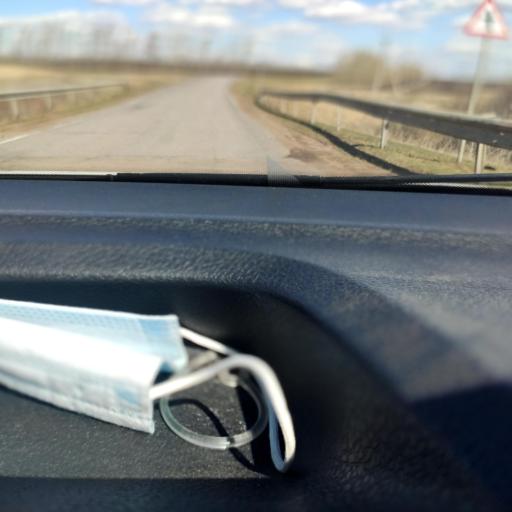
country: RU
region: Bashkortostan
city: Alekseyevka
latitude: 54.7789
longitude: 55.1774
